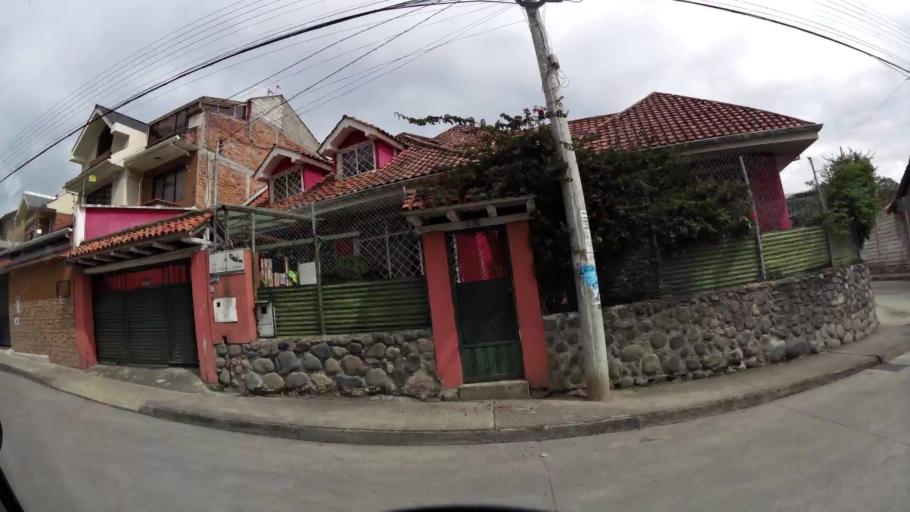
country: EC
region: Azuay
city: Cuenca
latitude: -2.9172
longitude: -79.0112
